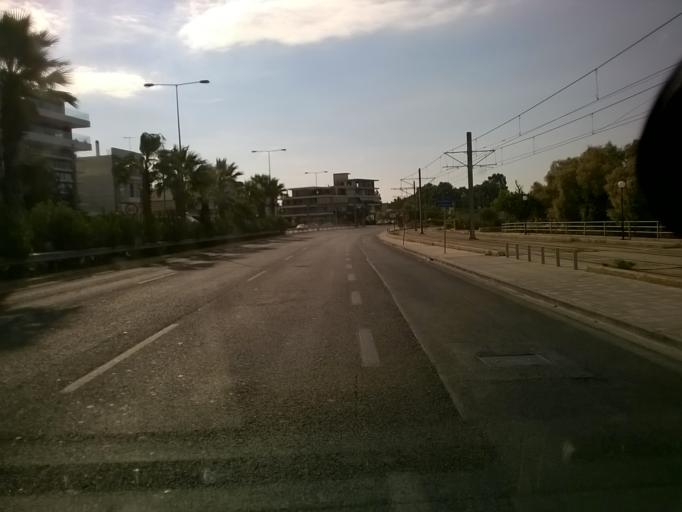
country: GR
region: Attica
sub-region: Nomarchia Athinas
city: Alimos
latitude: 37.9045
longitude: 23.7188
